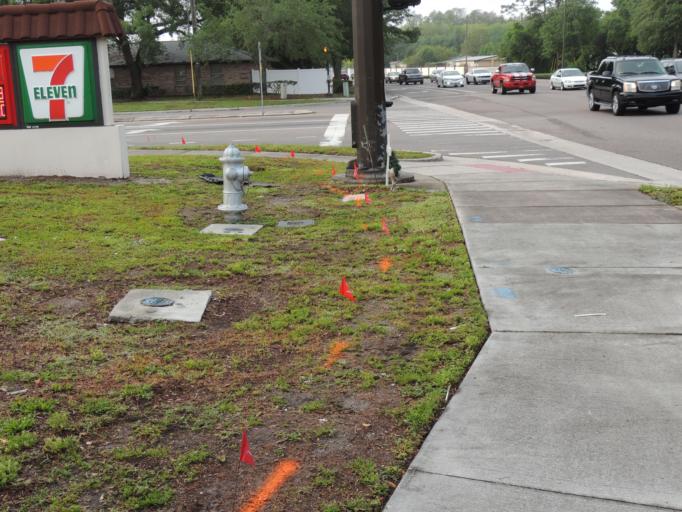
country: US
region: Florida
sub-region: Osceola County
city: Saint Cloud
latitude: 28.2282
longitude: -81.3176
